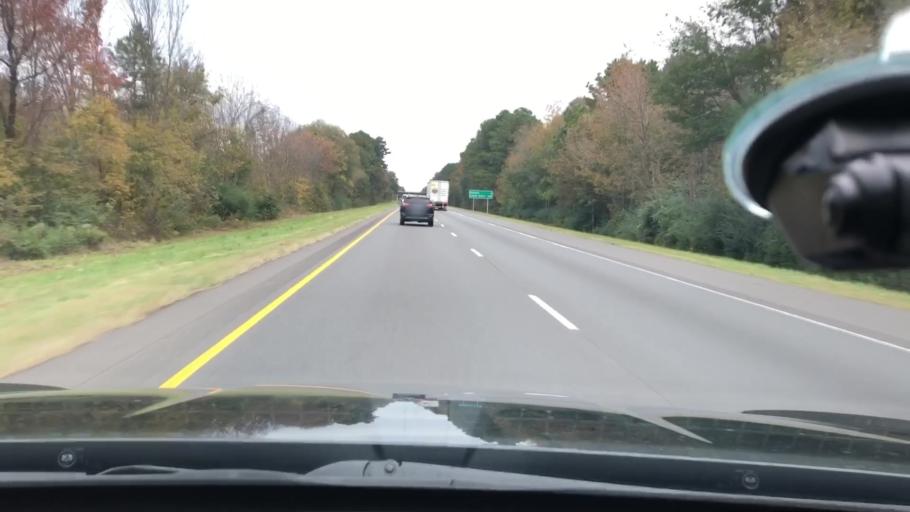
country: US
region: Arkansas
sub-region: Hempstead County
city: Hope
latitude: 33.6990
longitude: -93.5870
